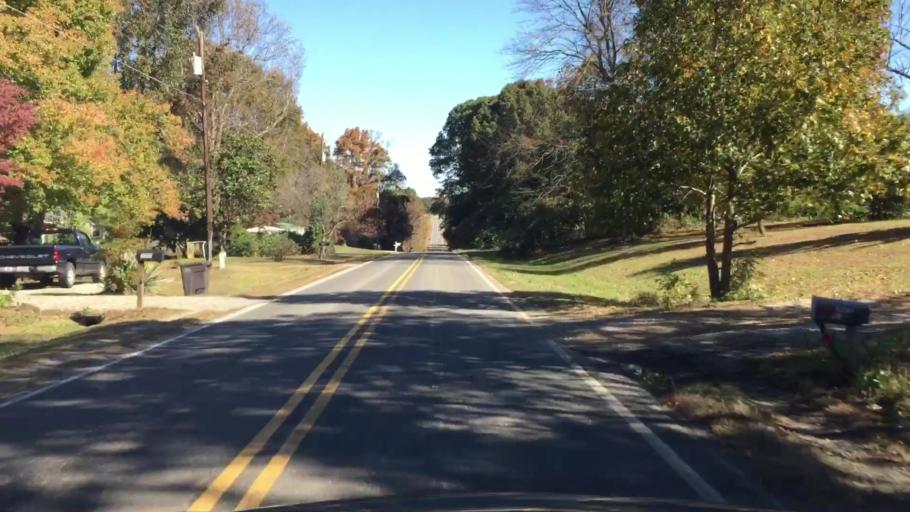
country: US
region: North Carolina
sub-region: Iredell County
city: Mooresville
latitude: 35.5713
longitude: -80.7694
